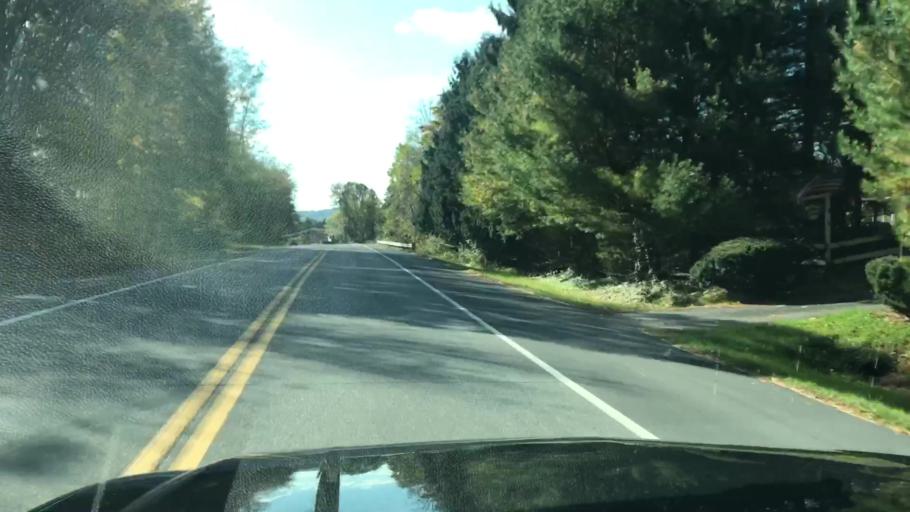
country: US
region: Pennsylvania
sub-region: Cumberland County
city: Lower Allen
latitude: 40.1626
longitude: -76.8852
